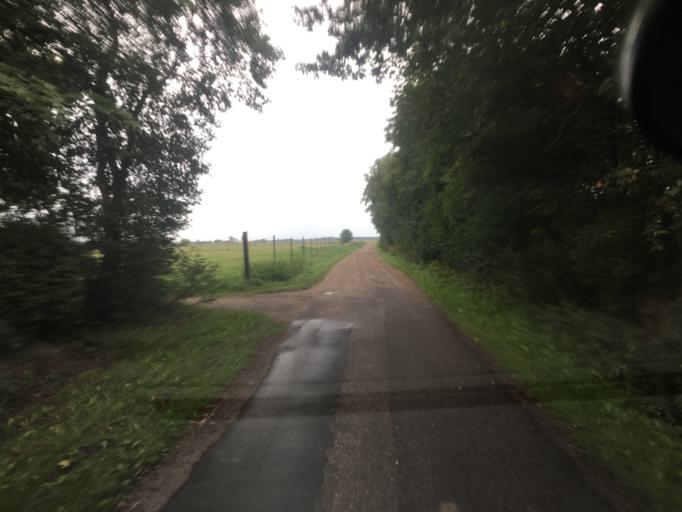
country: DK
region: South Denmark
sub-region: Tonder Kommune
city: Tonder
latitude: 54.9770
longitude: 8.9312
